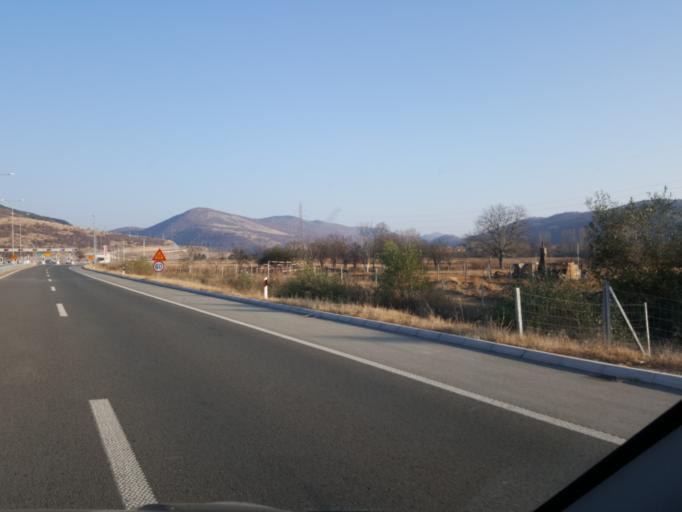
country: RS
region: Central Serbia
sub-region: Pirotski Okrug
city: Dimitrovgrad
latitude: 43.0225
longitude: 22.7323
